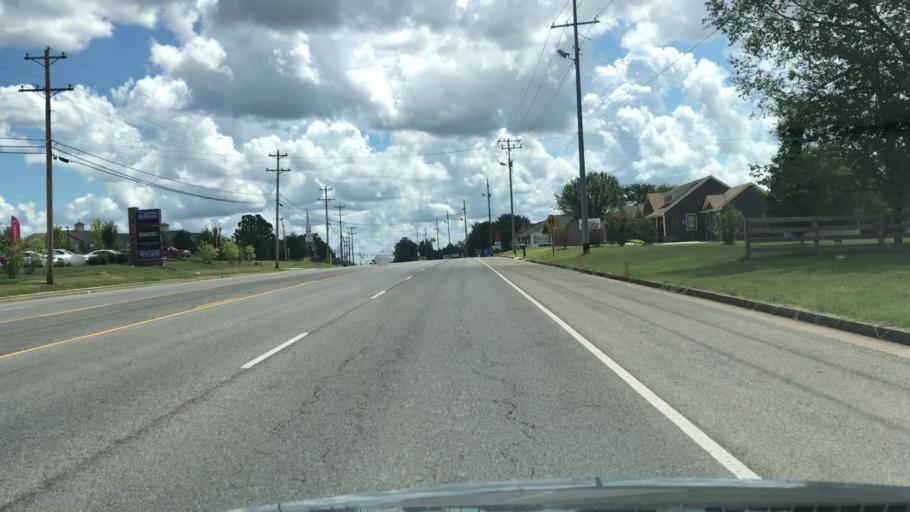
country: US
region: Tennessee
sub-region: Rutherford County
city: Murfreesboro
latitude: 35.8447
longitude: -86.4570
